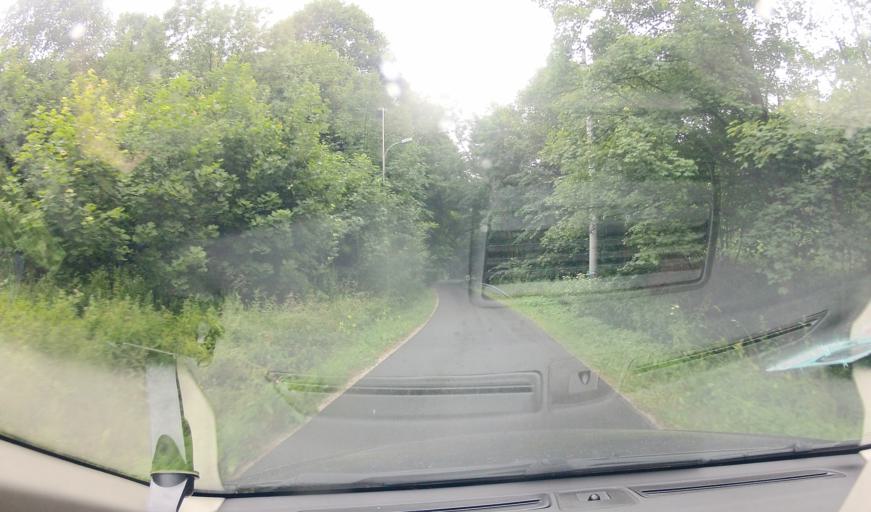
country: PL
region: Lower Silesian Voivodeship
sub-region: Powiat klodzki
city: Miedzylesie
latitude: 50.1193
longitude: 16.6413
